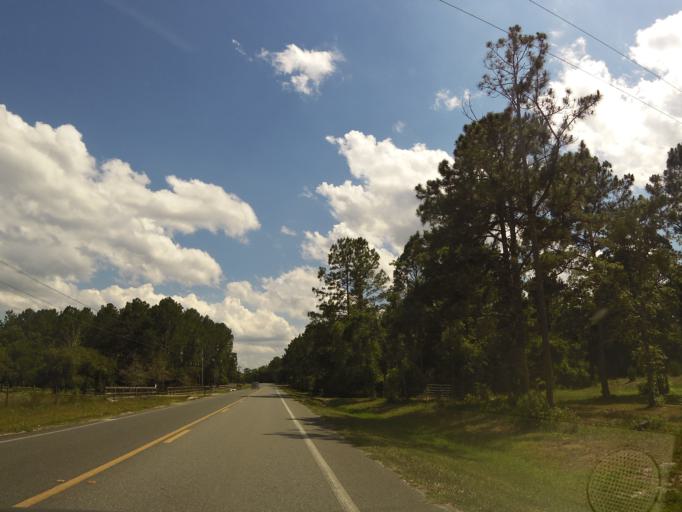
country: US
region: Florida
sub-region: Clay County
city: Keystone Heights
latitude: 29.8408
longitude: -81.9214
